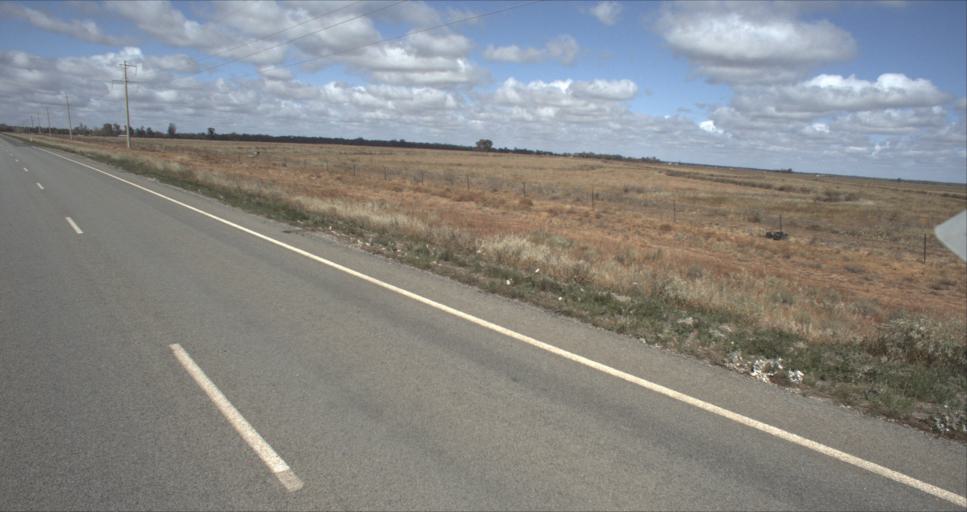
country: AU
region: New South Wales
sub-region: Murrumbidgee Shire
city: Darlington Point
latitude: -34.5819
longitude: 146.1649
